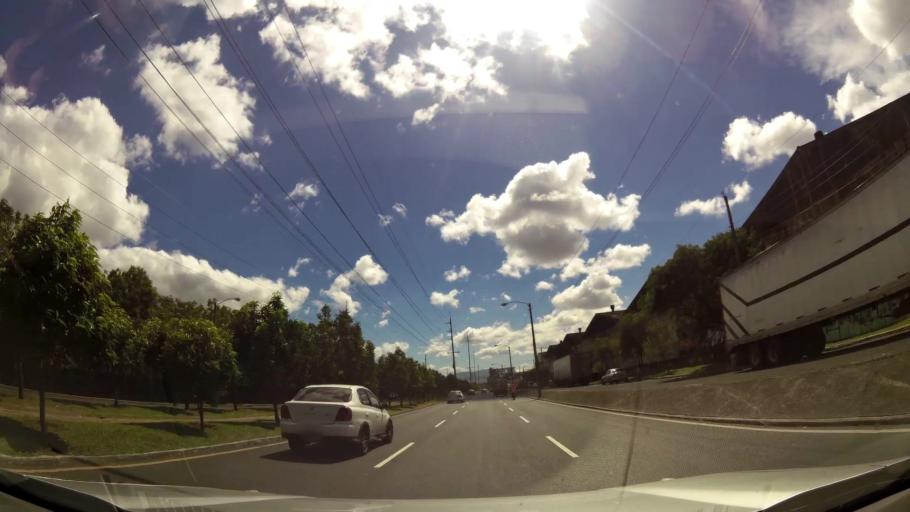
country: GT
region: Guatemala
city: Santa Catarina Pinula
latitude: 14.5763
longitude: -90.5426
